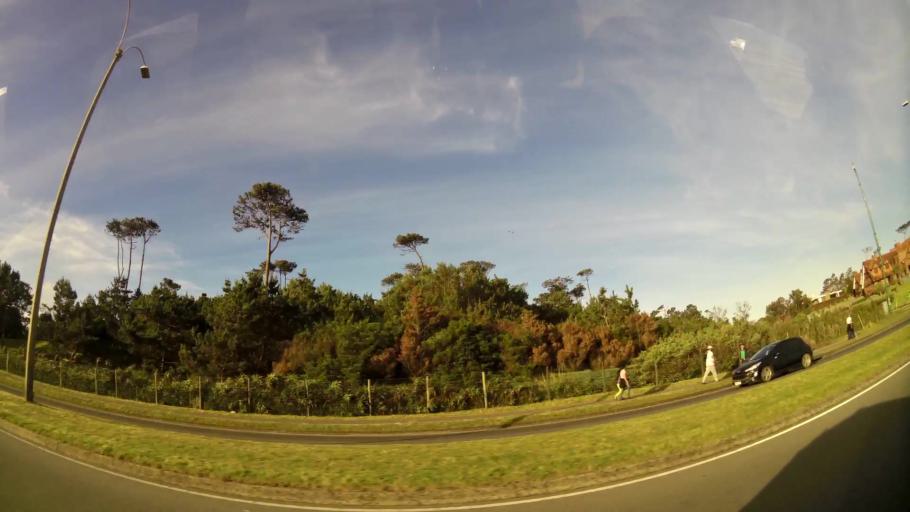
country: UY
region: Maldonado
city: Maldonado
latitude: -34.9134
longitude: -54.9856
